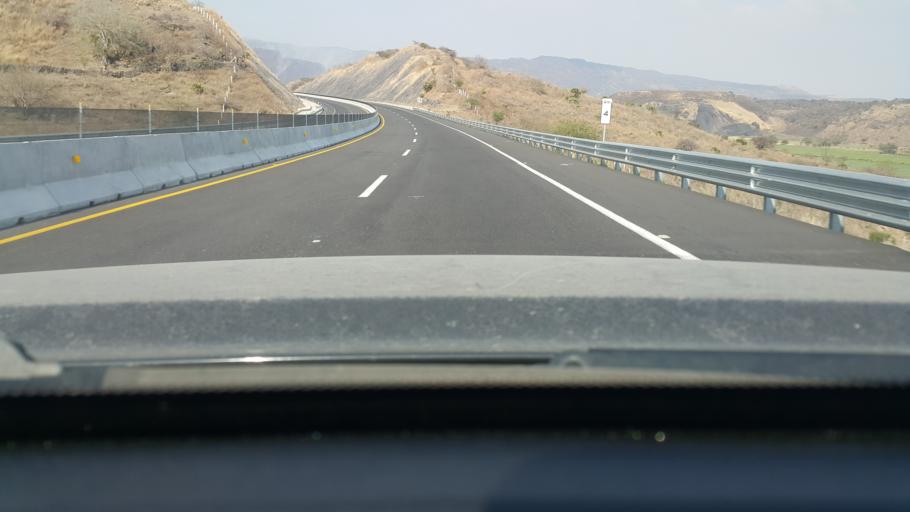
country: MX
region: Nayarit
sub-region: Ahuacatlan
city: Ahuacatlan
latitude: 21.0677
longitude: -104.4625
